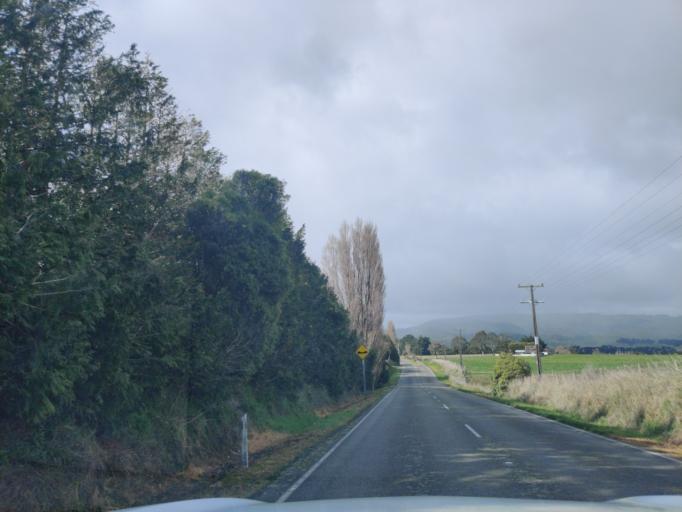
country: NZ
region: Manawatu-Wanganui
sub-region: Palmerston North City
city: Palmerston North
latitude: -40.2940
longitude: 175.7344
